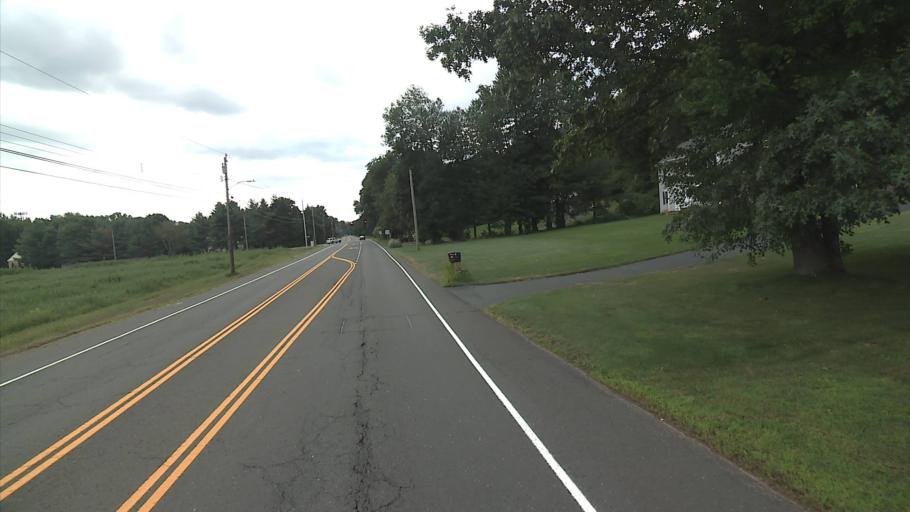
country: US
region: Connecticut
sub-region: Hartford County
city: Tariffville
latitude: 41.8794
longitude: -72.7442
